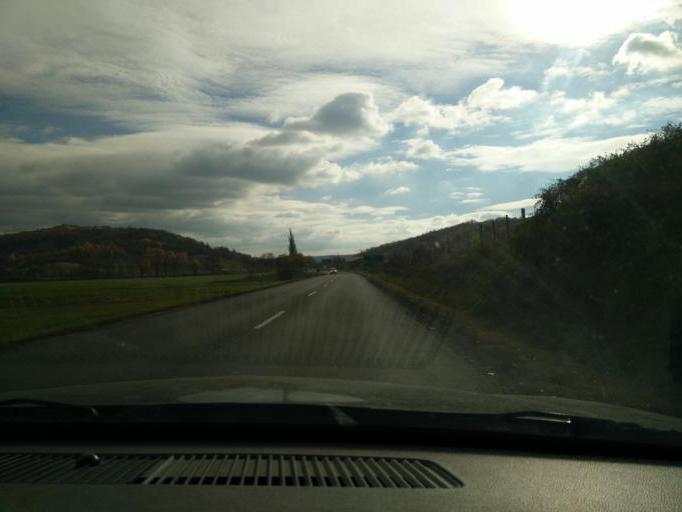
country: HU
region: Komarom-Esztergom
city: Piliscsev
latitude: 47.6741
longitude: 18.7788
